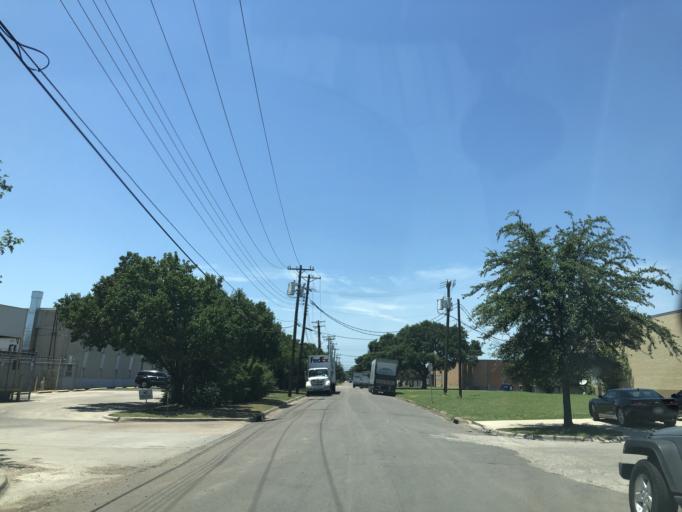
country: US
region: Texas
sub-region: Dallas County
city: Irving
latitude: 32.8145
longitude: -96.8880
